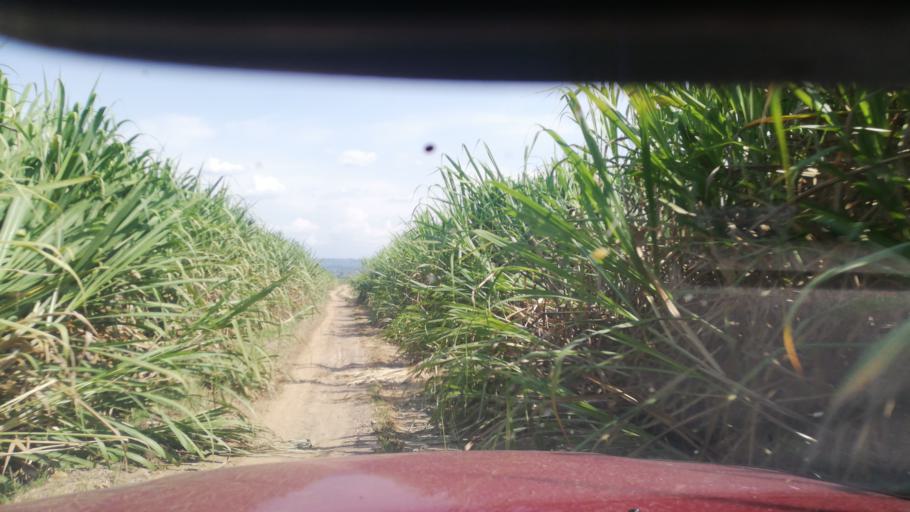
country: CO
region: Risaralda
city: La Virginia
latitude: 4.8995
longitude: -75.9303
